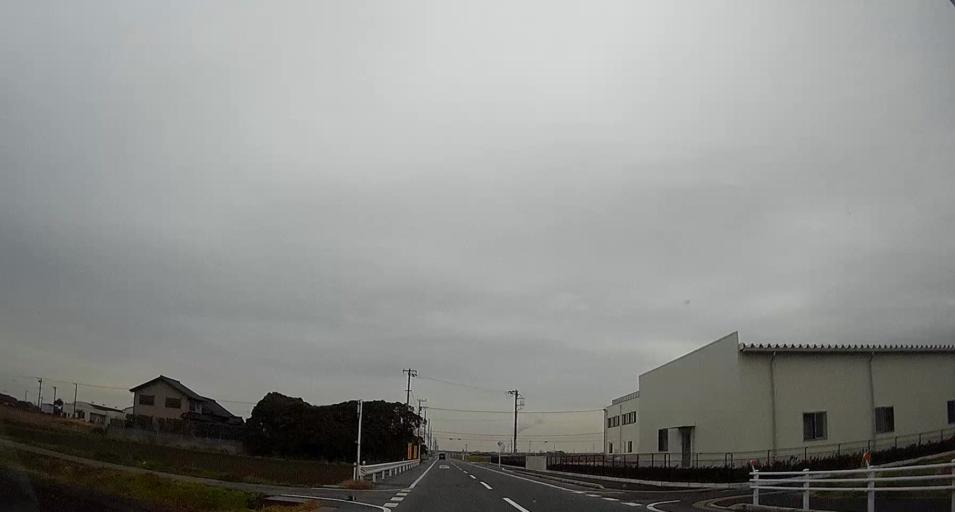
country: JP
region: Chiba
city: Kisarazu
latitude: 35.4269
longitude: 139.9127
